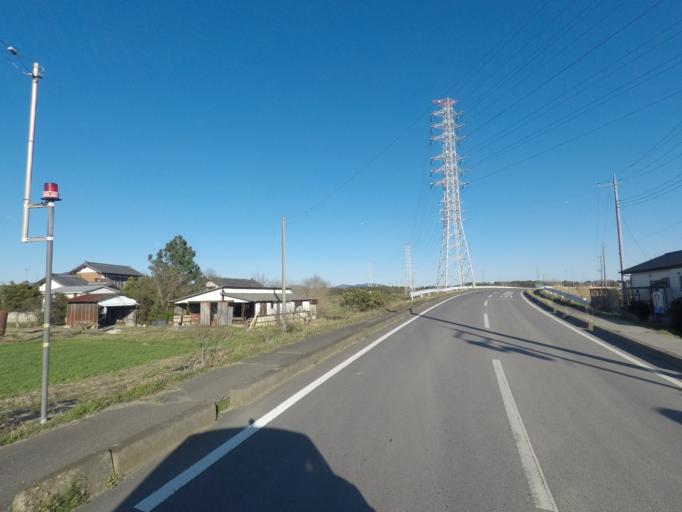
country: JP
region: Ibaraki
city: Ishige
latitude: 36.1772
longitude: 140.0084
